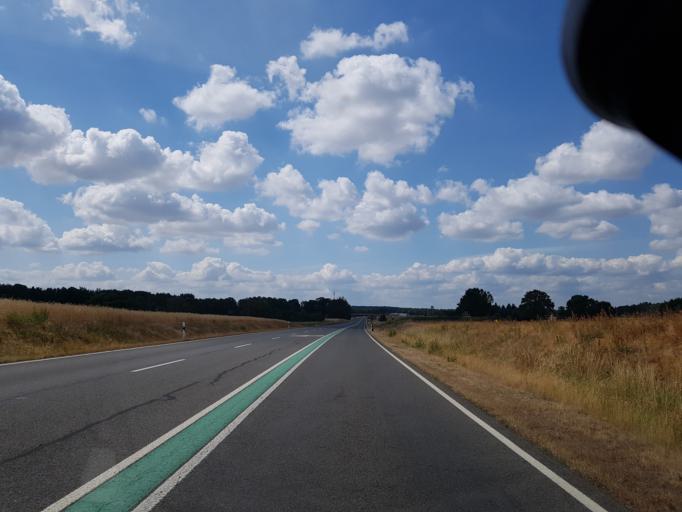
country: DE
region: Brandenburg
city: Drebkau
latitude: 51.6522
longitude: 14.2422
